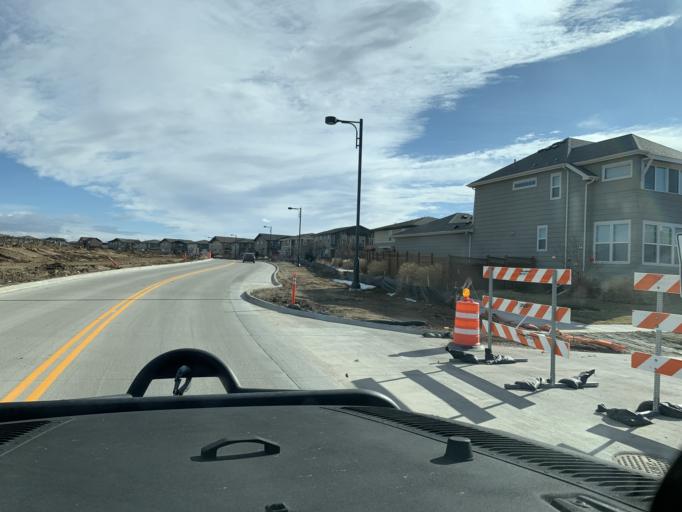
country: US
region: Colorado
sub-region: Adams County
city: Aurora
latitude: 39.7587
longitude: -104.8636
